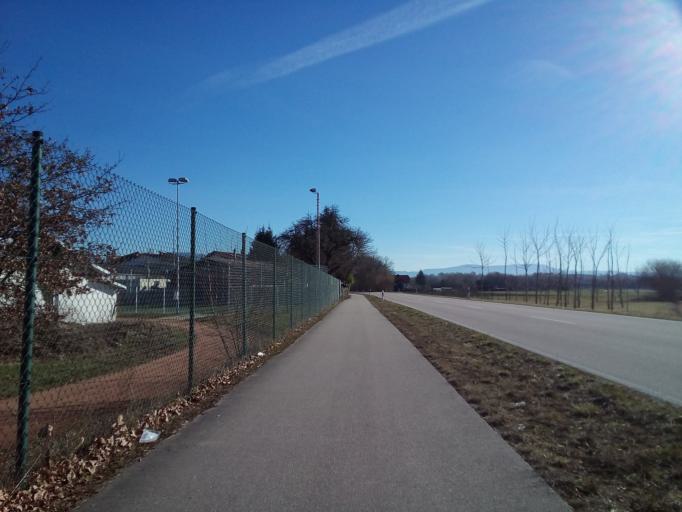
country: DE
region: Baden-Wuerttemberg
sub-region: Freiburg Region
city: Renchen
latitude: 48.6110
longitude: 8.0201
